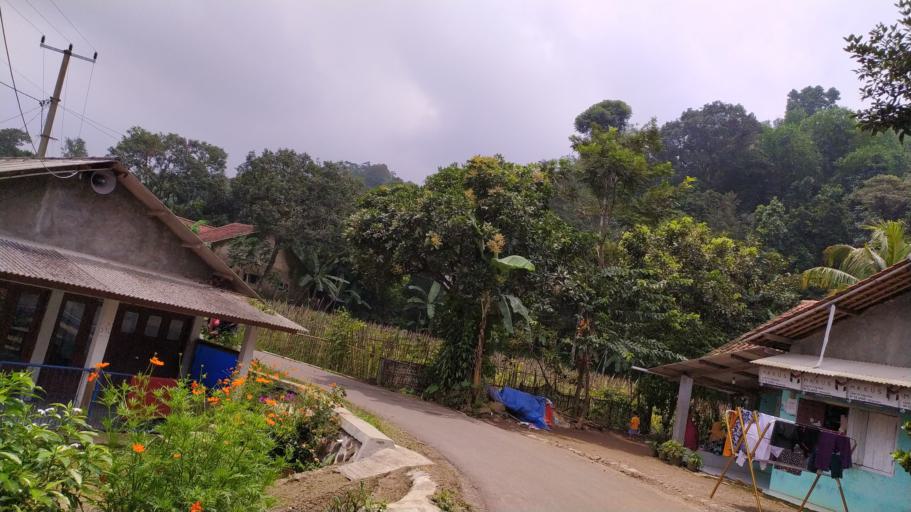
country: ID
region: West Java
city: Ciampea
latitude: -6.6252
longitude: 106.7127
